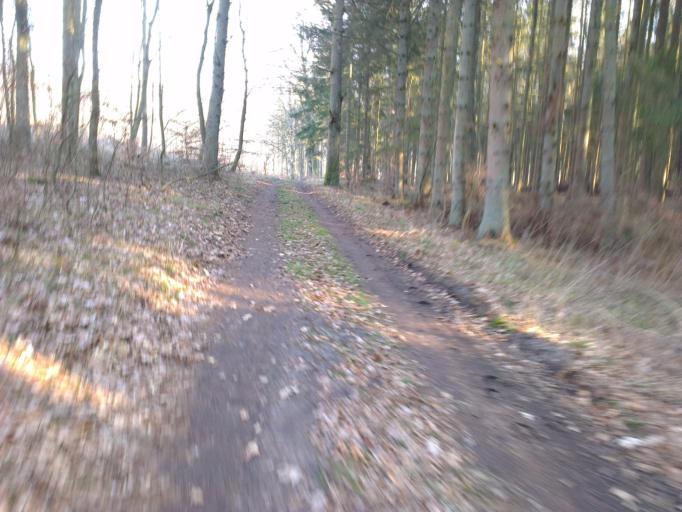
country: DK
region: Capital Region
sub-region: Frederikssund Kommune
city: Jaegerspris
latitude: 55.8799
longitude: 11.9942
